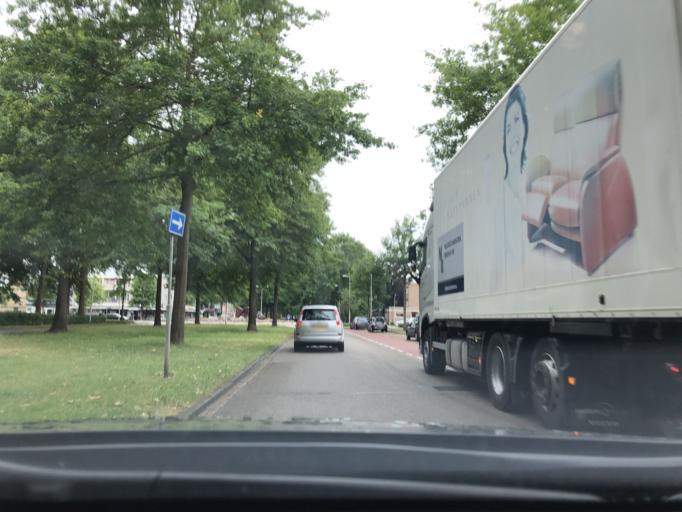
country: NL
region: North Brabant
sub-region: Gemeente Oss
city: Oss
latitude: 51.7712
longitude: 5.5163
